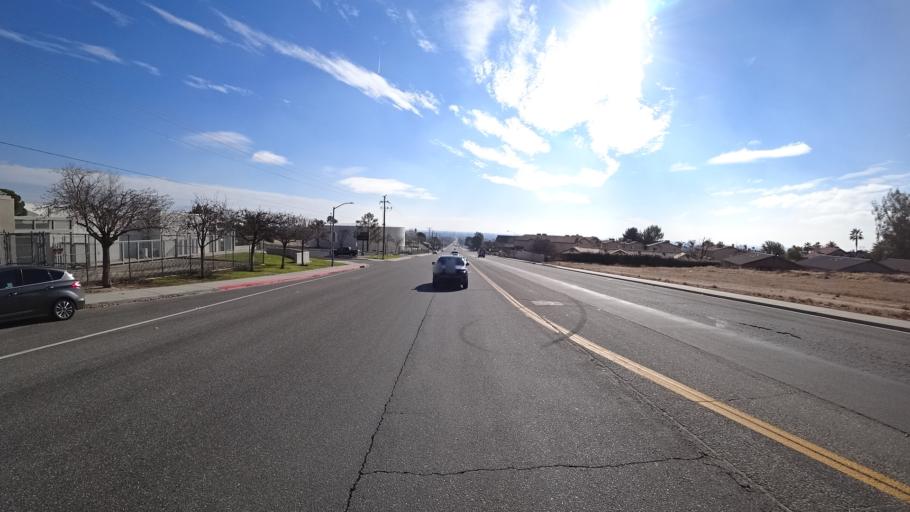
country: US
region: California
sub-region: Kern County
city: Bakersfield
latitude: 35.3828
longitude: -118.9142
